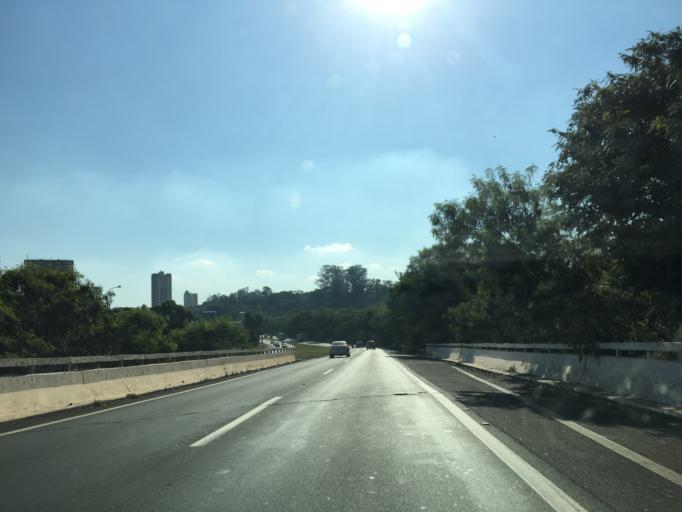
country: BR
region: Sao Paulo
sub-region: Piracicaba
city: Piracicaba
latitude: -22.7176
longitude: -47.6233
